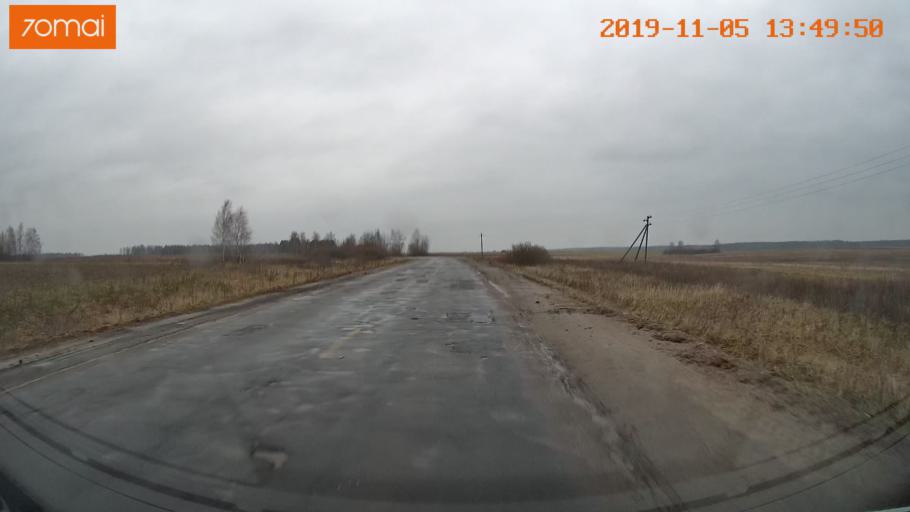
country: RU
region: Ivanovo
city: Kaminskiy
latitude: 57.0145
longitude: 41.4107
